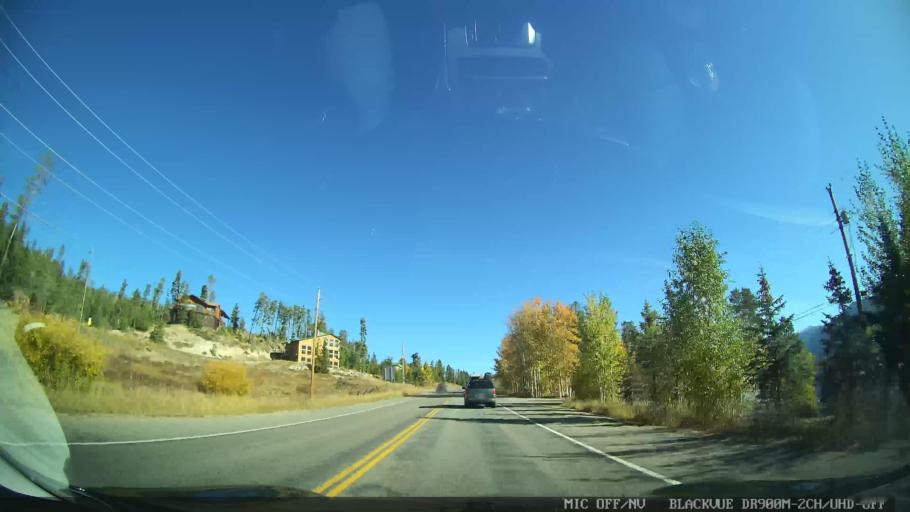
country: US
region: Colorado
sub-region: Grand County
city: Granby
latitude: 40.2356
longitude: -105.8476
